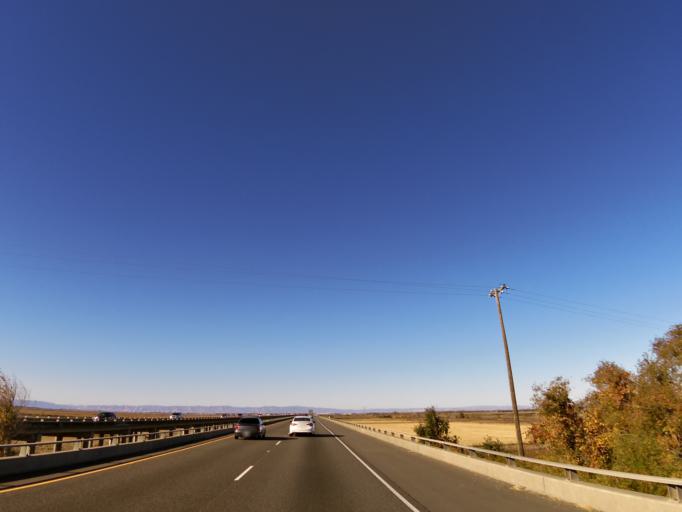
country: US
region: California
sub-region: Yolo County
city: Woodland
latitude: 38.6735
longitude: -121.6431
